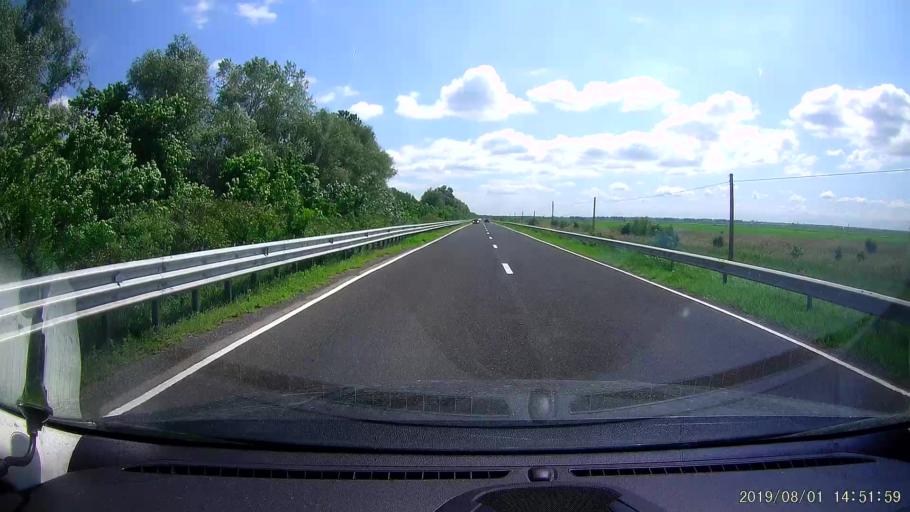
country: RO
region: Braila
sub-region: Comuna Vadeni
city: Vadeni
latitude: 45.3653
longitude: 28.0142
